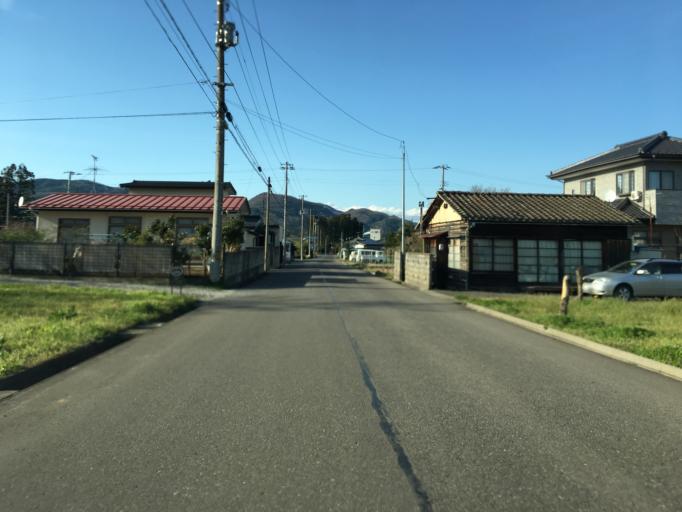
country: JP
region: Fukushima
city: Fukushima-shi
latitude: 37.7551
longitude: 140.3720
